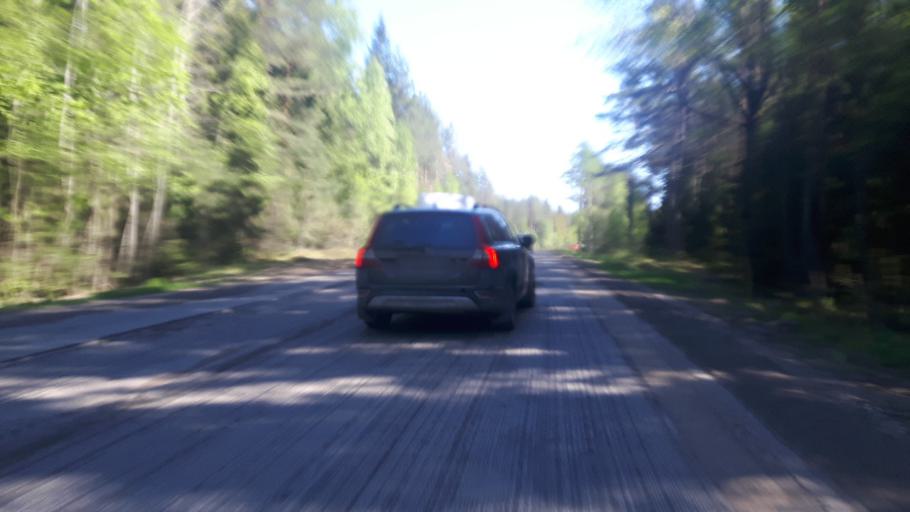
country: RU
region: Leningrad
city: Sosnovyy Bor
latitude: 60.2283
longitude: 29.0028
